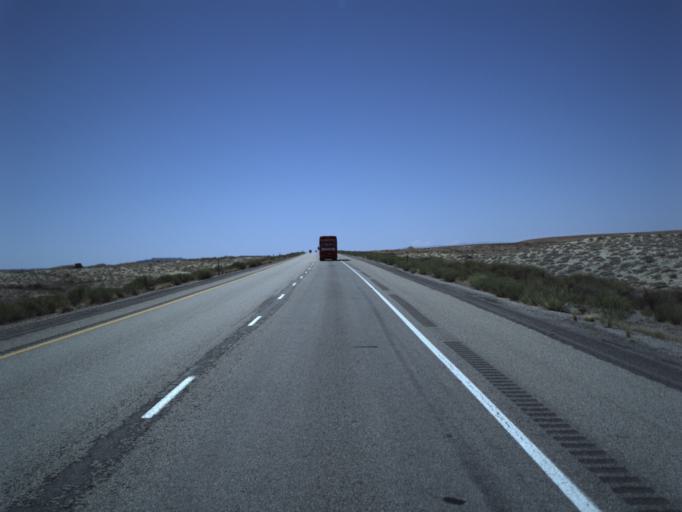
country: US
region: Utah
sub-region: Grand County
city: Moab
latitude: 38.9606
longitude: -109.3807
